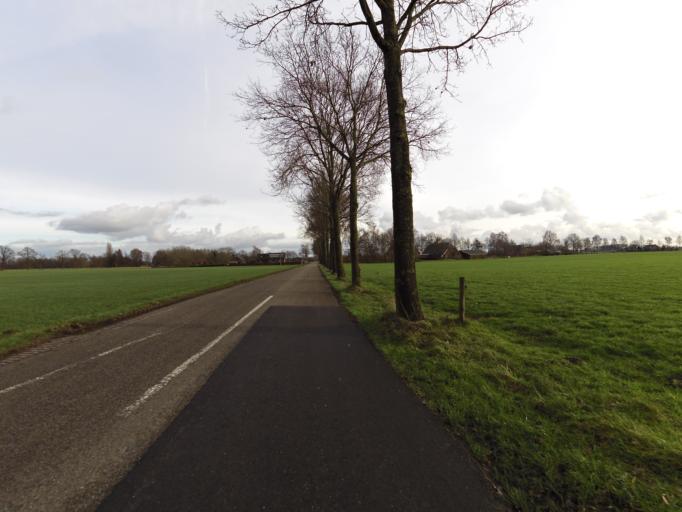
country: NL
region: Gelderland
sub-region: Oude IJsselstreek
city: Wisch
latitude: 51.9751
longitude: 6.4002
